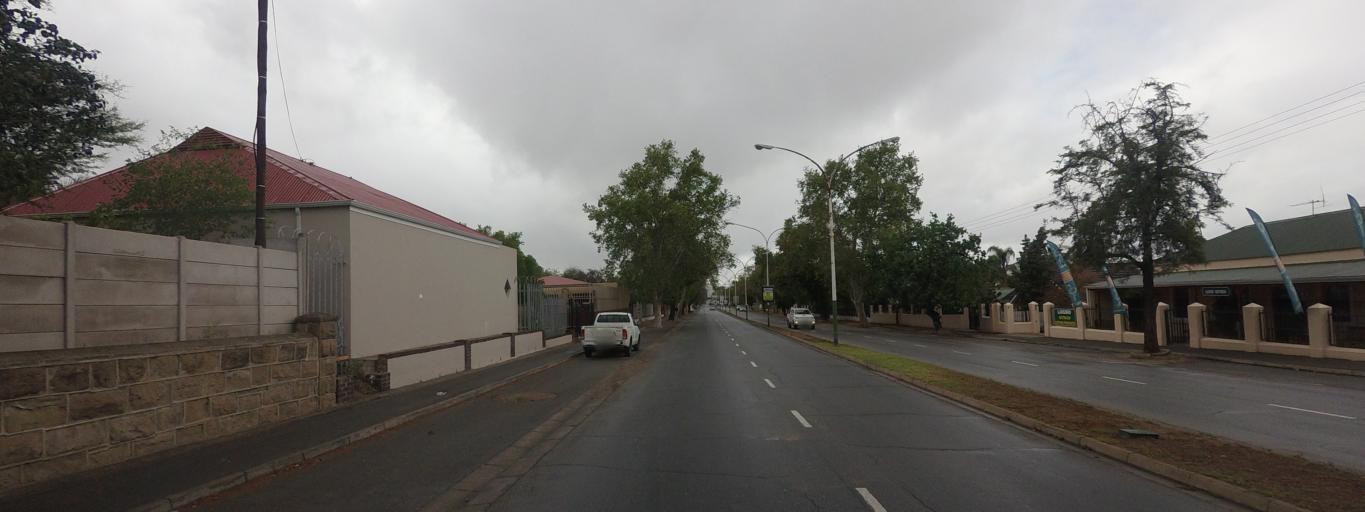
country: ZA
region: Western Cape
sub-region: Eden District Municipality
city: Oudtshoorn
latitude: -33.5985
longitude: 22.2059
